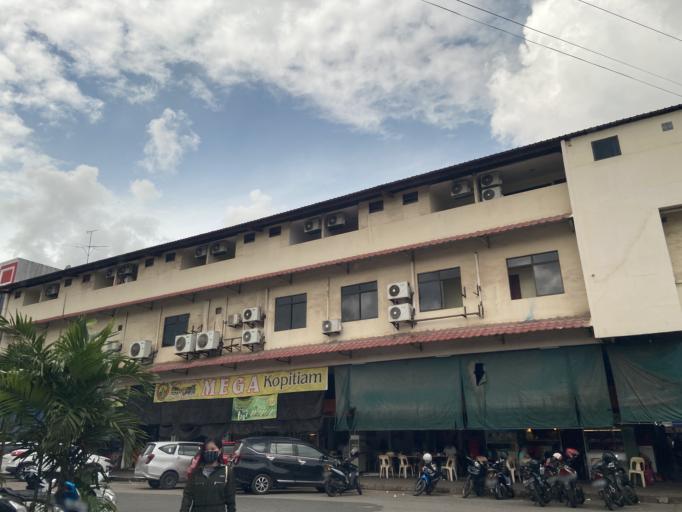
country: SG
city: Singapore
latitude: 1.1358
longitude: 104.0099
